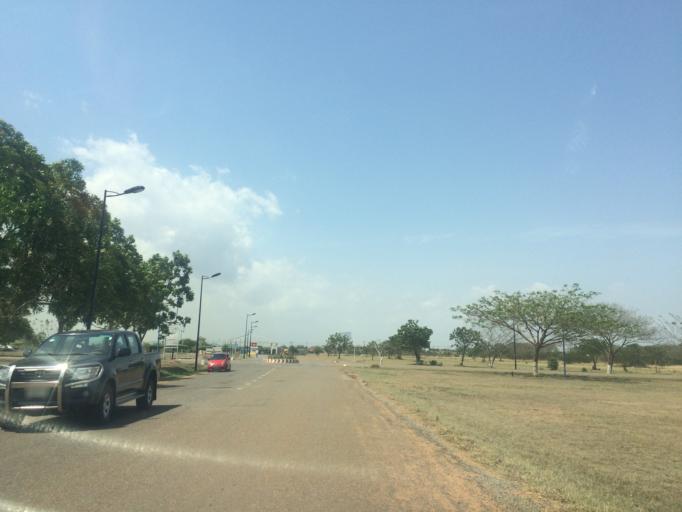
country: GH
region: Greater Accra
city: Tema
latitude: 5.7718
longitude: 0.0833
